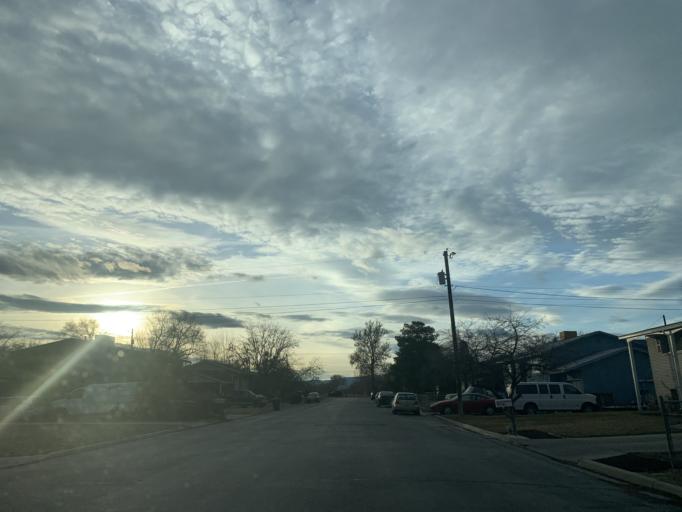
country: US
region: Utah
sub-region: Utah County
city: Provo
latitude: 40.2235
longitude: -111.6761
